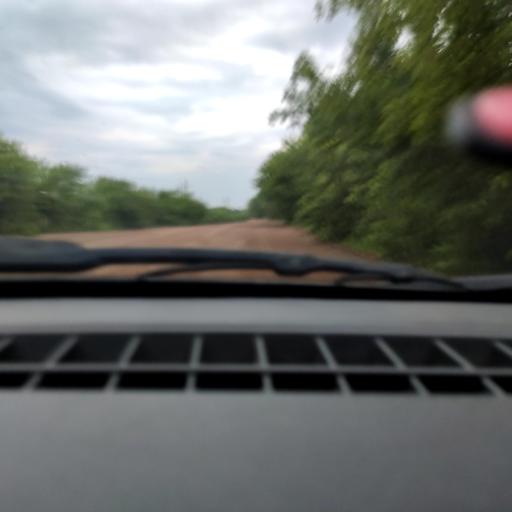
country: RU
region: Bashkortostan
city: Blagoveshchensk
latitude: 54.9170
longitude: 55.9842
